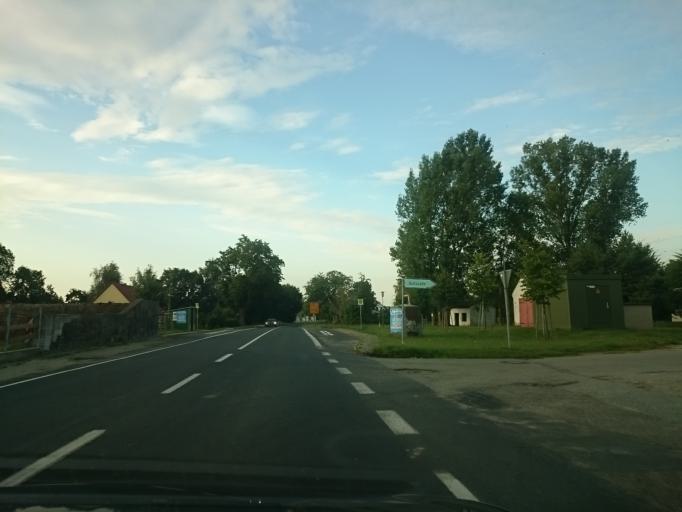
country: DE
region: Mecklenburg-Vorpommern
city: Gross Kiesow
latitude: 53.9489
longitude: 13.4902
